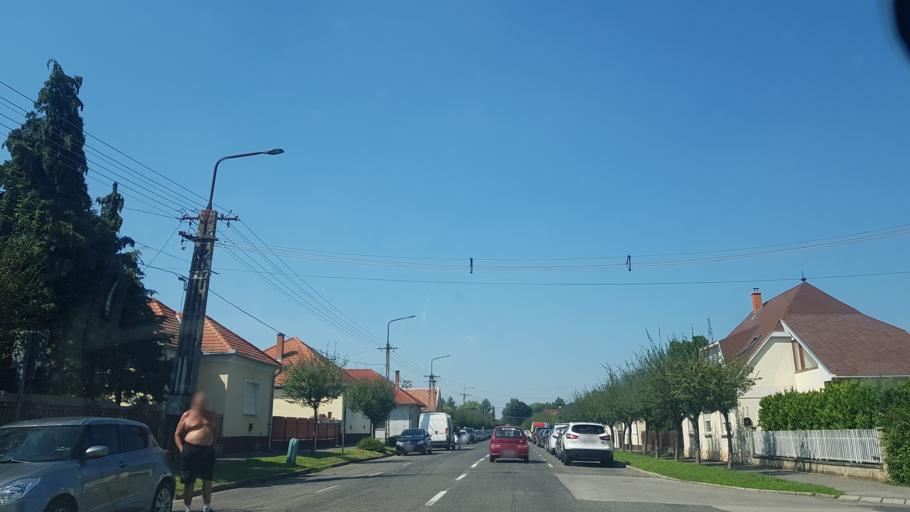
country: HU
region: Somogy
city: Nagyatad
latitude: 46.2336
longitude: 17.3609
